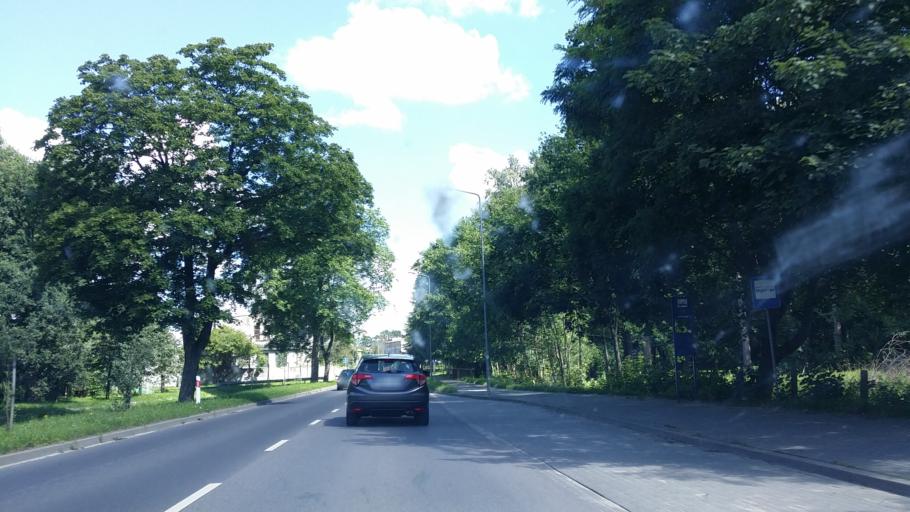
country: PL
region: West Pomeranian Voivodeship
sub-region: Powiat swidwinski
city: Swidwin
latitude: 53.7656
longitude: 15.7729
